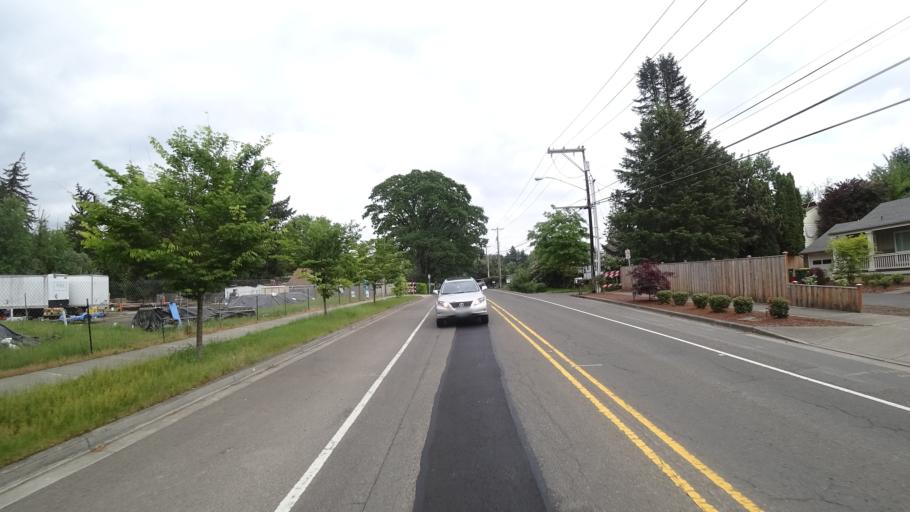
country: US
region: Oregon
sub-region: Washington County
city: Raleigh Hills
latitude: 45.4694
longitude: -122.7783
